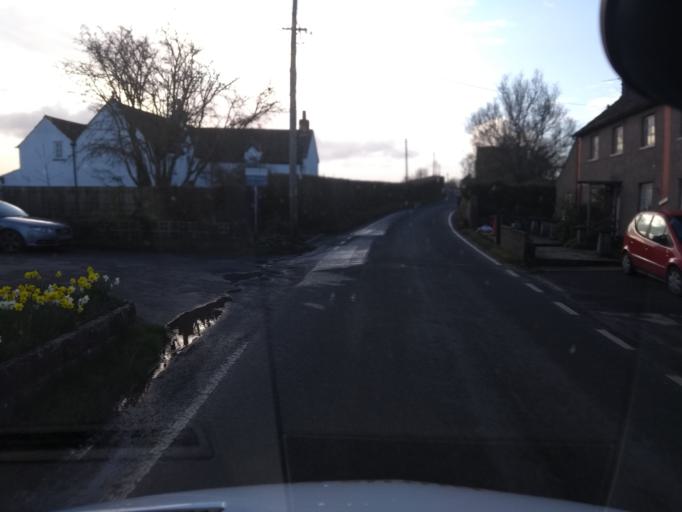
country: GB
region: England
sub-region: Somerset
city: Wedmore
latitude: 51.2233
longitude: -2.7939
